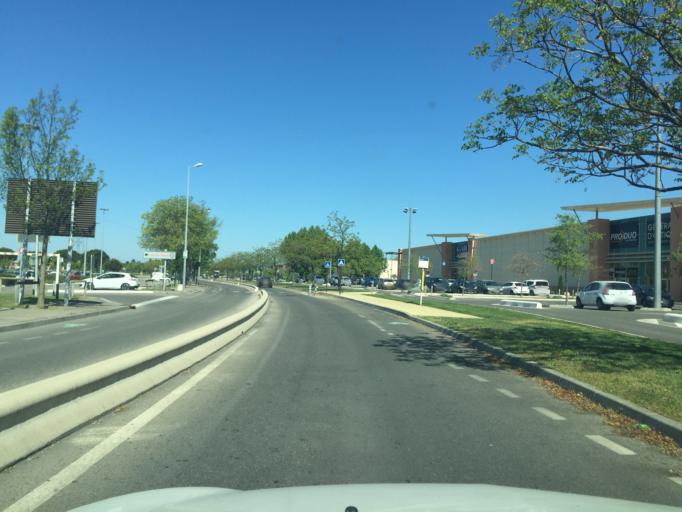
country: FR
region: Provence-Alpes-Cote d'Azur
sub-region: Departement du Vaucluse
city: Montfavet
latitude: 43.9226
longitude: 4.8673
